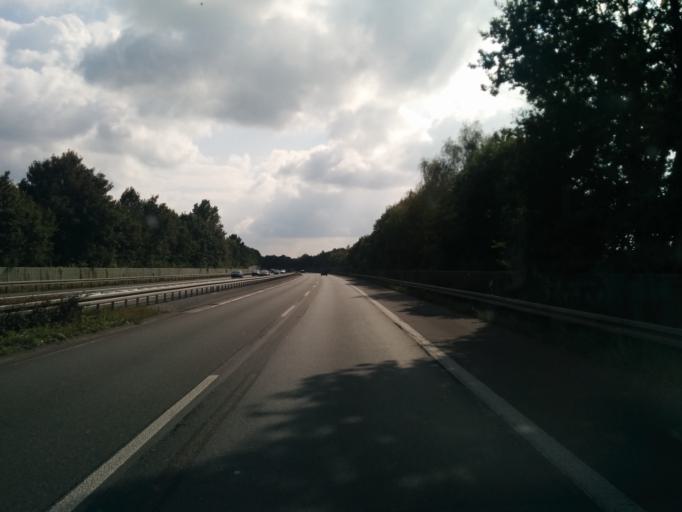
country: DE
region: North Rhine-Westphalia
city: Marl
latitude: 51.6698
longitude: 7.1567
